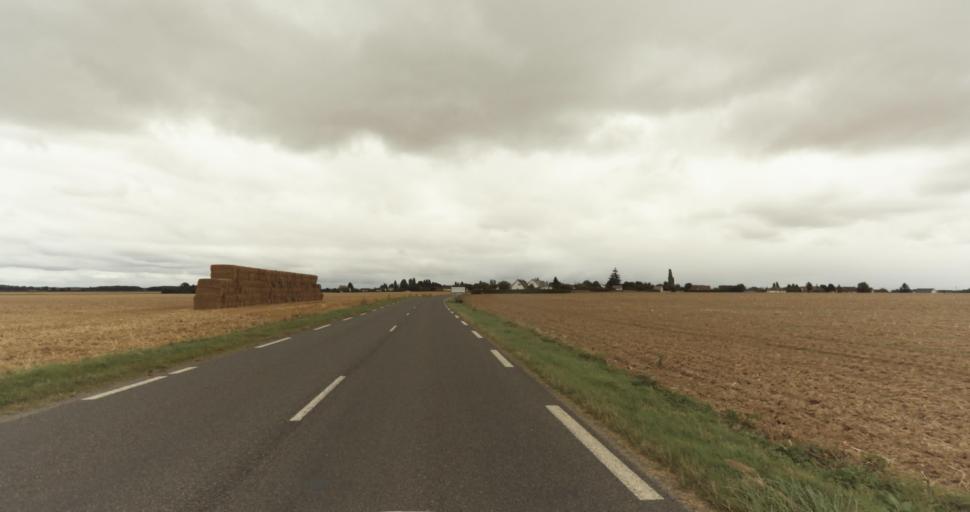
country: FR
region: Haute-Normandie
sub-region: Departement de l'Eure
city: Evreux
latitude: 48.9699
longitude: 1.2042
